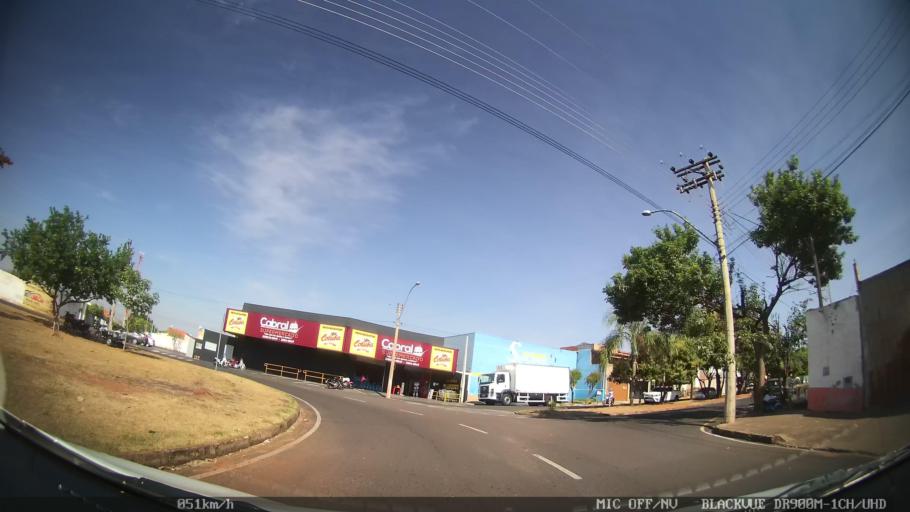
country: BR
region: Sao Paulo
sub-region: Sao Jose Do Rio Preto
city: Sao Jose do Rio Preto
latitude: -20.7928
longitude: -49.4333
